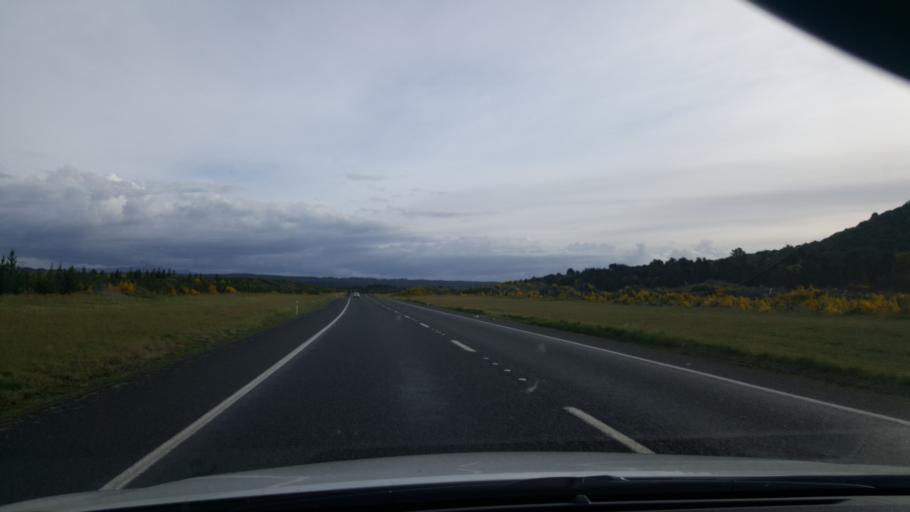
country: NZ
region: Waikato
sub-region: Taupo District
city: Taupo
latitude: -38.8465
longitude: 176.0577
